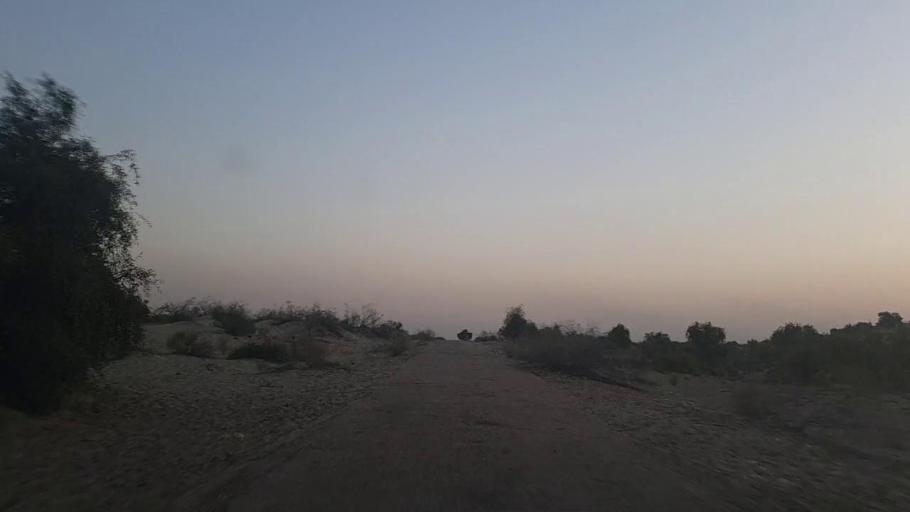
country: PK
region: Sindh
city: Jam Sahib
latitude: 26.4087
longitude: 68.8095
